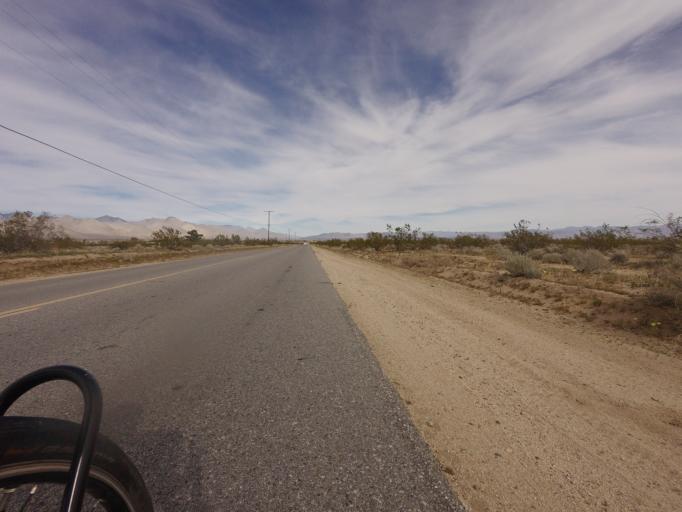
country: US
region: California
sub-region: Kern County
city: Inyokern
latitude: 35.6925
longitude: -117.8258
